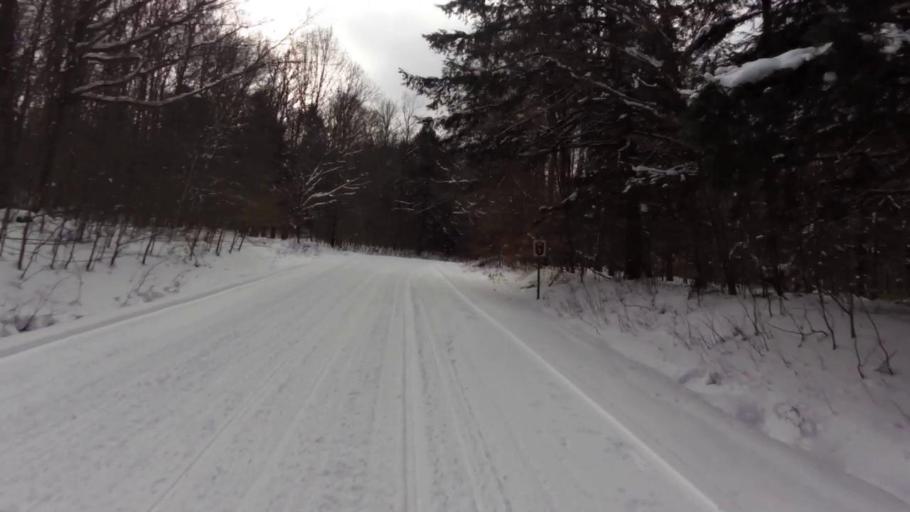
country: US
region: New York
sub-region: Cattaraugus County
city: Salamanca
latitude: 42.0719
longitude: -78.7541
